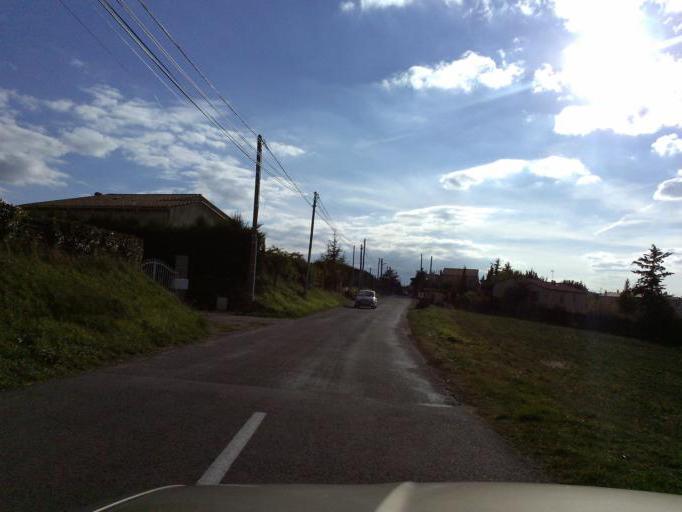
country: FR
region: Provence-Alpes-Cote d'Azur
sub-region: Departement des Alpes-de-Haute-Provence
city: Valensole
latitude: 43.8425
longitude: 5.9852
